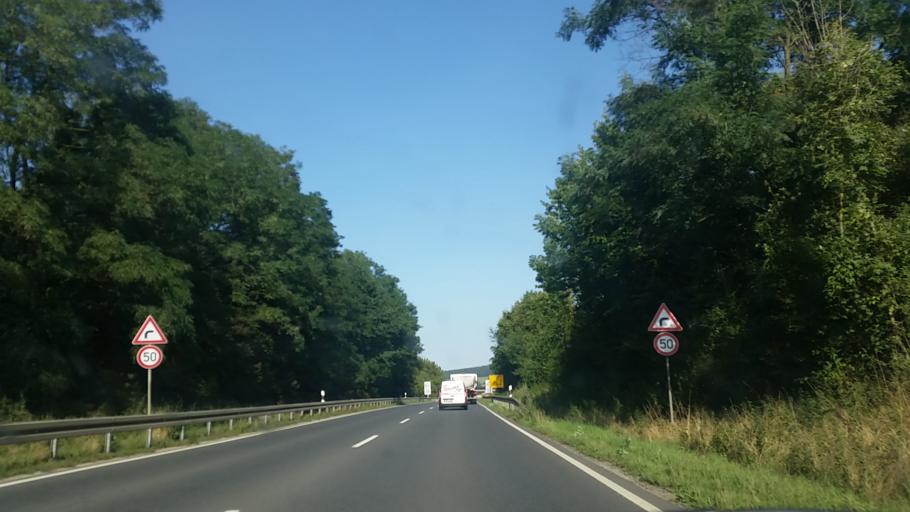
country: DE
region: Lower Saxony
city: Coppenbrugge
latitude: 52.1206
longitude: 9.5279
